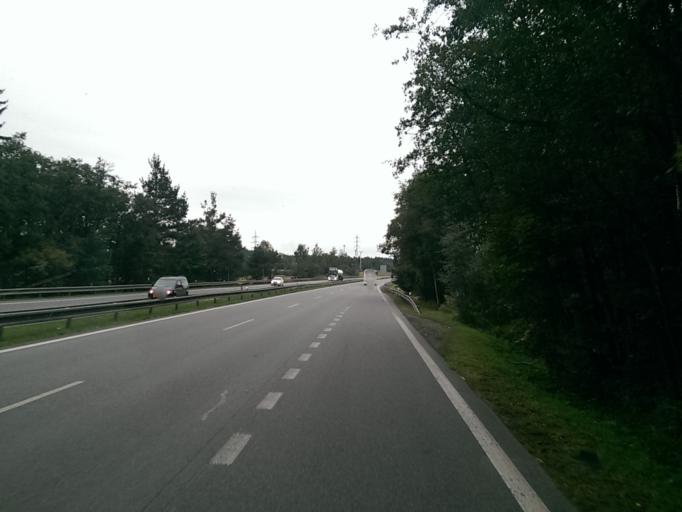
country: CZ
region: Vysocina
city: Dobronin
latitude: 49.4481
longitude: 15.6108
